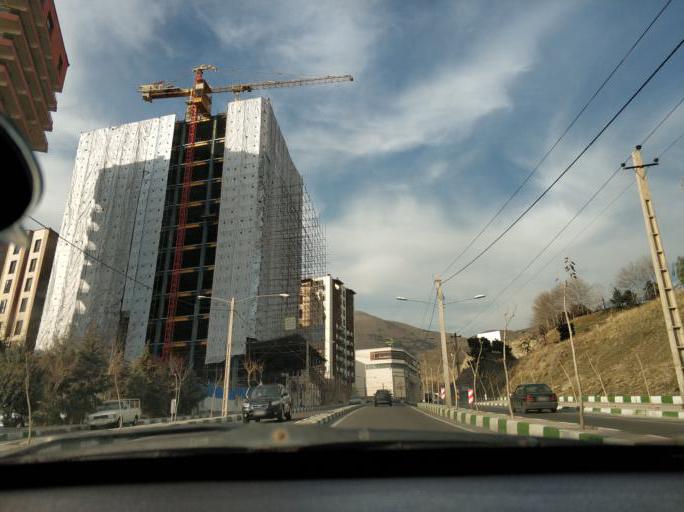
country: IR
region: Tehran
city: Tajrish
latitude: 35.8133
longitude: 51.4848
